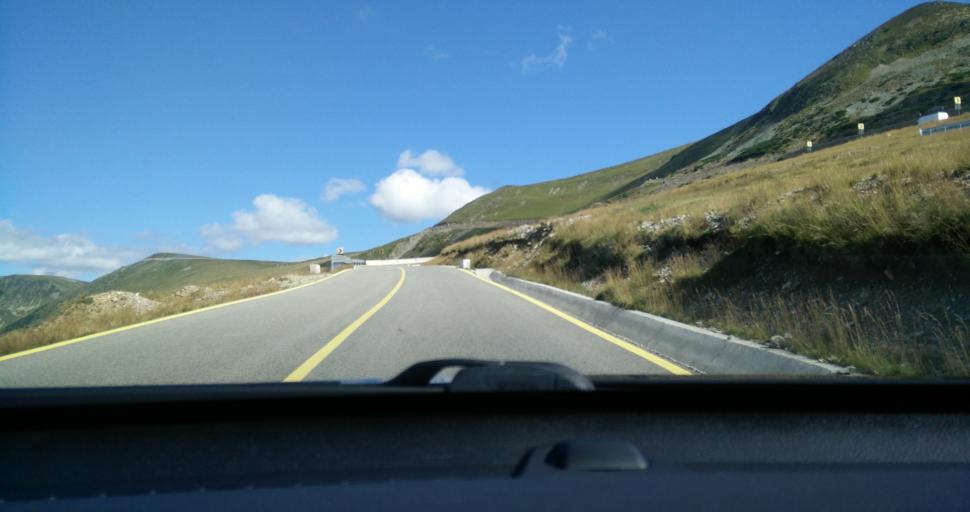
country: RO
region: Gorj
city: Novaci-Straini
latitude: 45.3164
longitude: 23.6810
